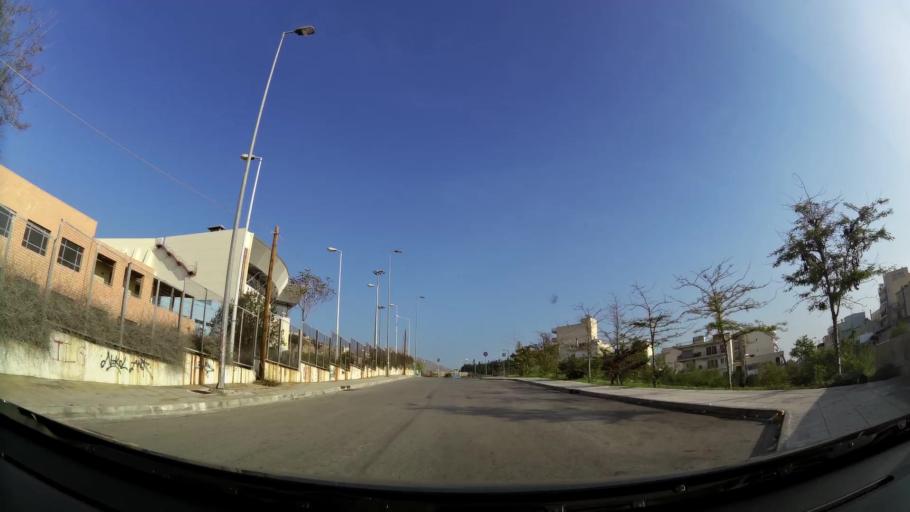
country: GR
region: Attica
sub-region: Nomos Piraios
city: Nikaia
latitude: 37.9697
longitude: 23.6350
